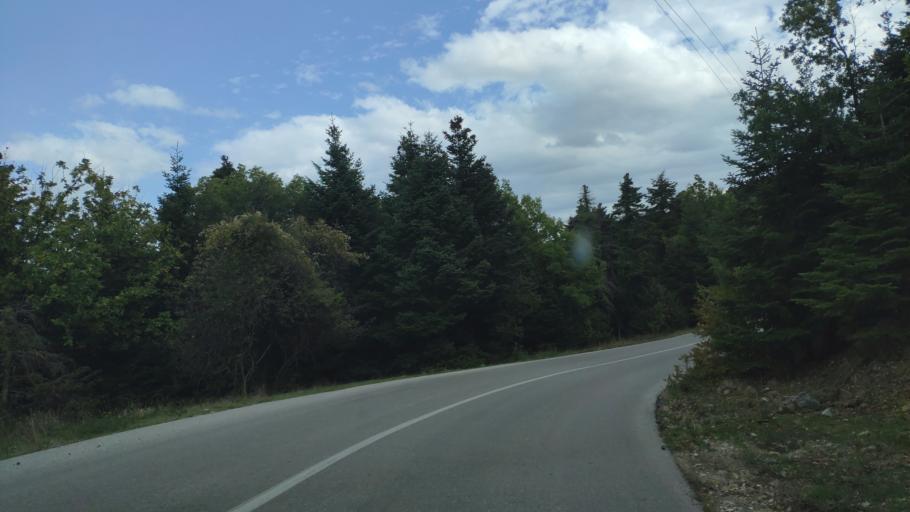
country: GR
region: Central Greece
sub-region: Nomos Fthiotidos
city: Anthili
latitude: 38.7378
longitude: 22.3803
